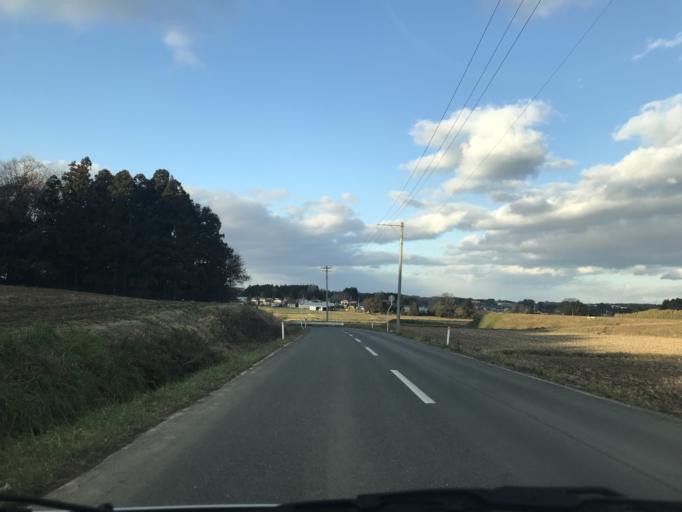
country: JP
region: Miyagi
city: Kogota
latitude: 38.6361
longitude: 141.0539
